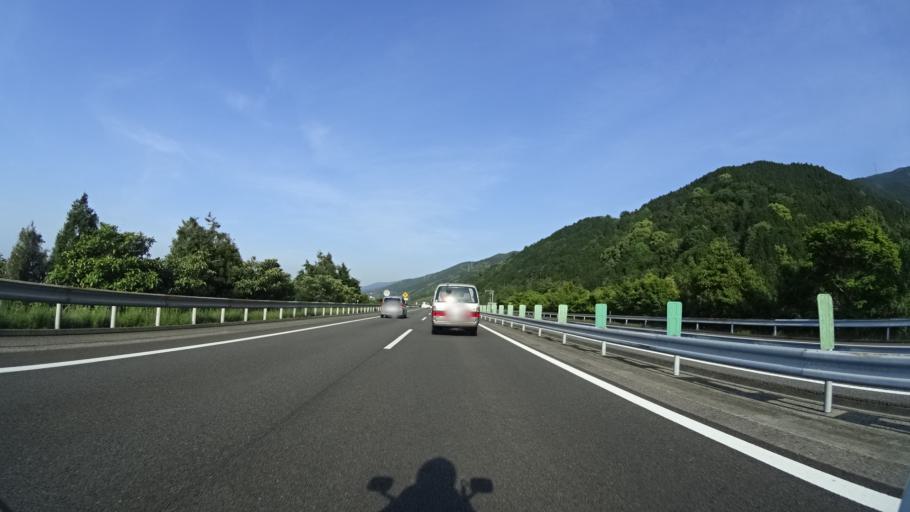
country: JP
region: Ehime
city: Kawanoecho
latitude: 33.9609
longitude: 133.5032
